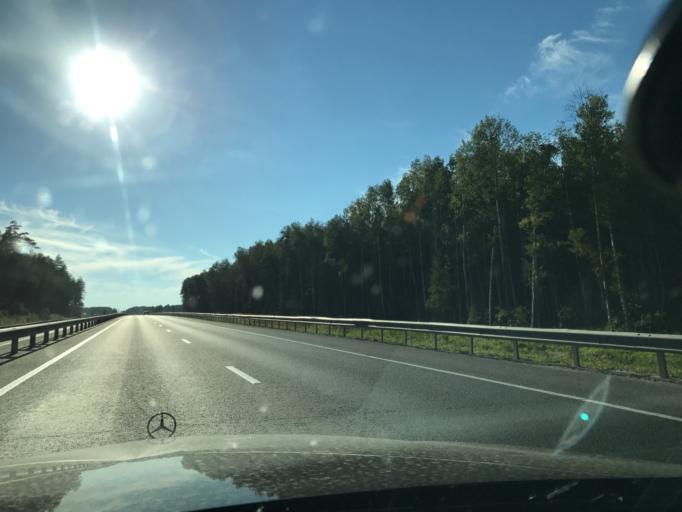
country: RU
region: Vladimir
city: Stepantsevo
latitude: 56.2338
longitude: 41.8211
